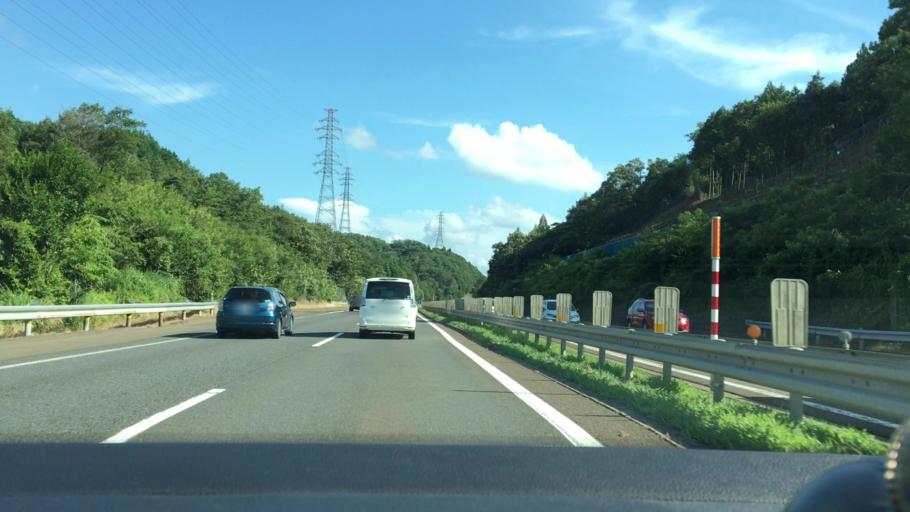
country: JP
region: Fukui
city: Maruoka
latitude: 36.2242
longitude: 136.2812
